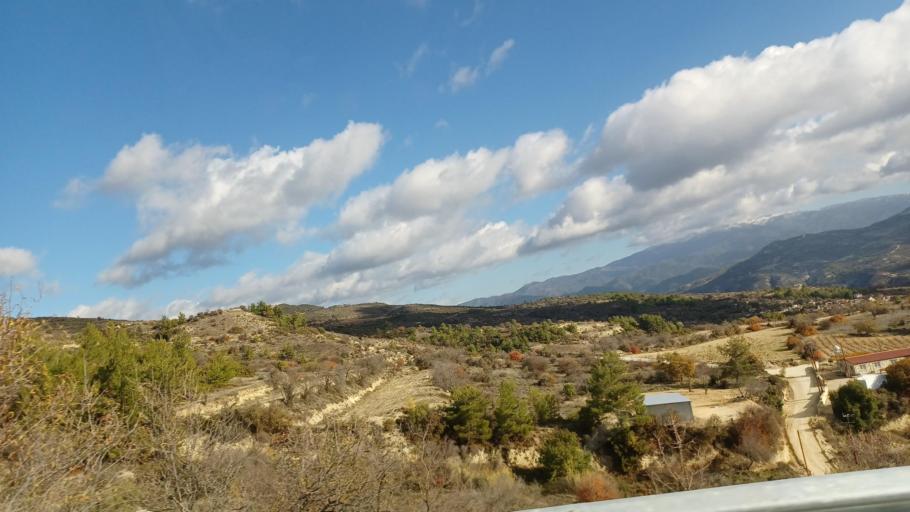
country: CY
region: Limassol
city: Pachna
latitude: 34.8438
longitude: 32.6938
